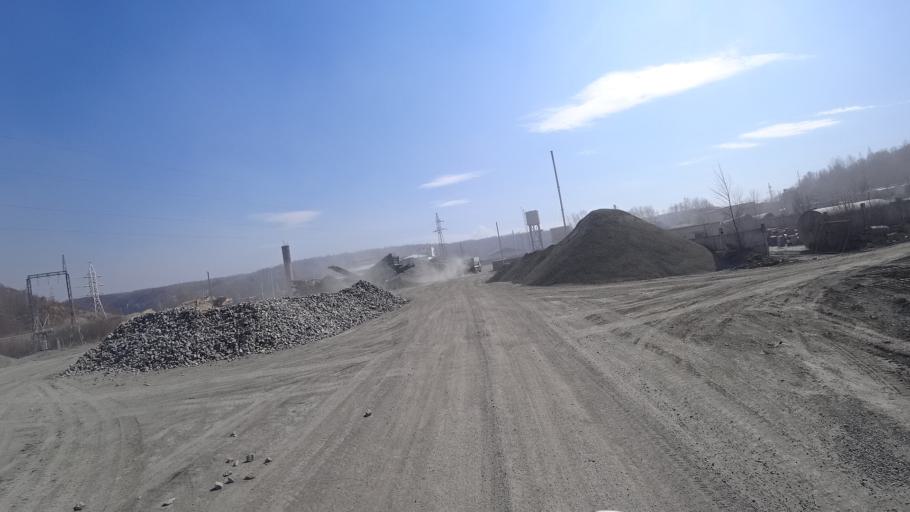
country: RU
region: Amur
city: Novobureyskiy
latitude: 49.7918
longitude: 129.9620
